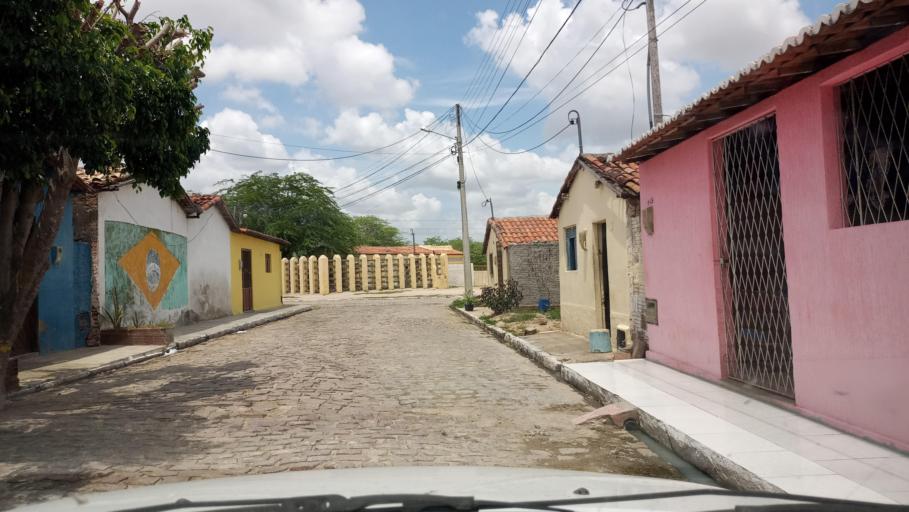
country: BR
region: Rio Grande do Norte
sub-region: Tangara
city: Tangara
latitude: -6.1040
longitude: -35.7138
